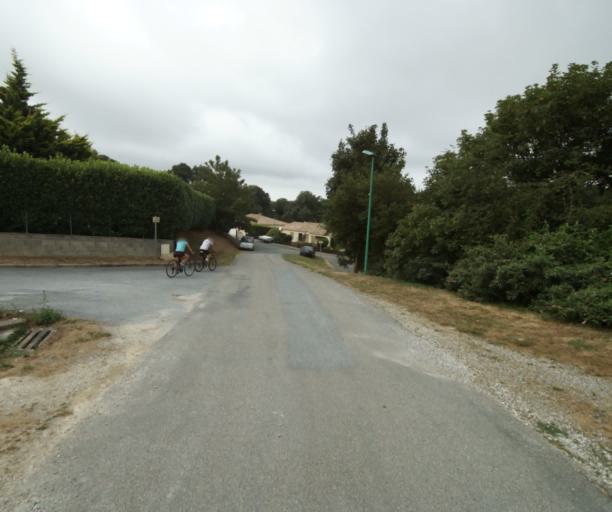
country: FR
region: Midi-Pyrenees
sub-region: Departement du Tarn
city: Soreze
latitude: 43.4085
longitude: 2.0791
